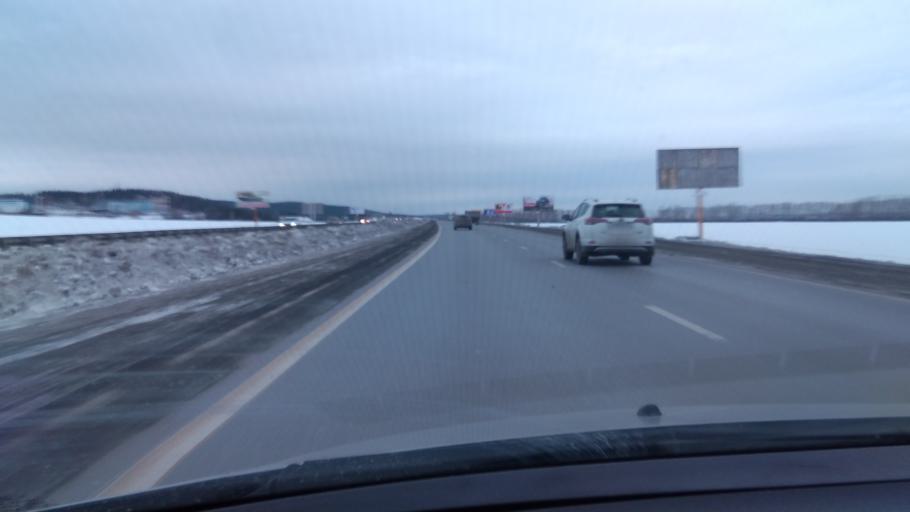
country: RU
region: Sverdlovsk
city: Aramil
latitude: 56.6868
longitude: 60.7705
